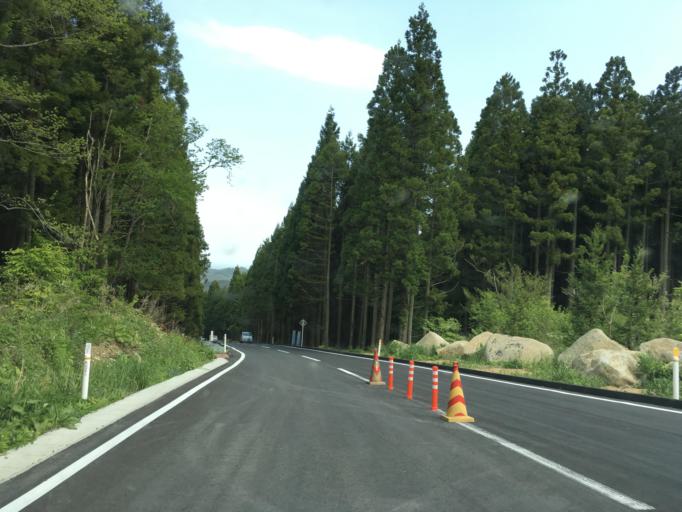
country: JP
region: Iwate
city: Ofunato
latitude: 38.8547
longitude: 141.4815
